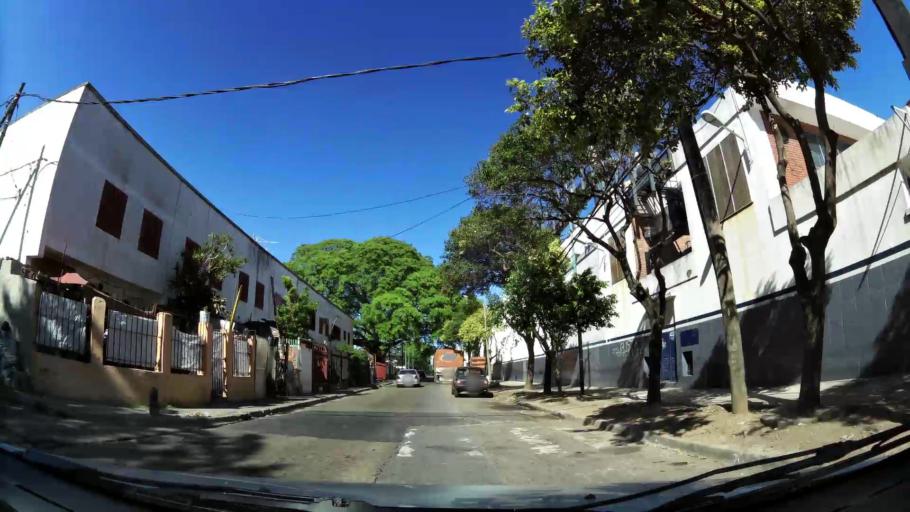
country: AR
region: Buenos Aires
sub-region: Partido de General San Martin
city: General San Martin
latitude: -34.5452
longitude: -58.5208
